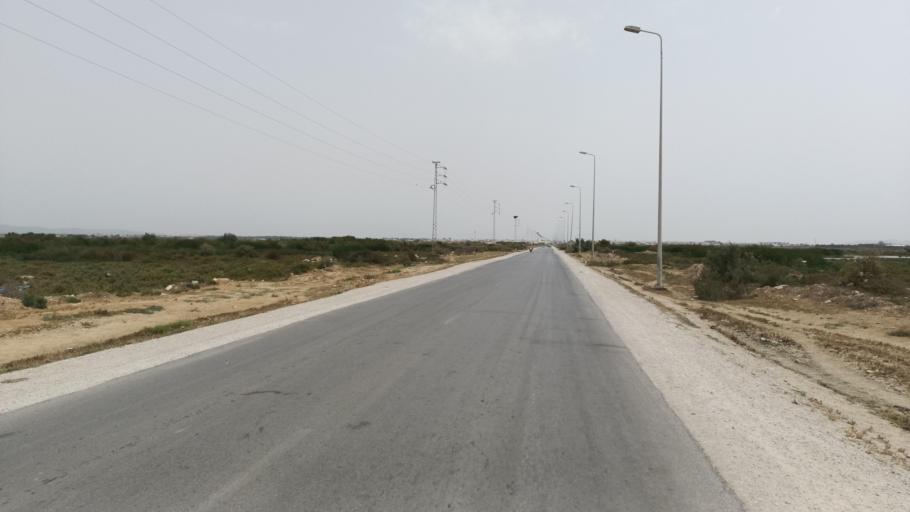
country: TN
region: Nabul
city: Manzil Bu Zalafah
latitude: 36.7245
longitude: 10.4713
